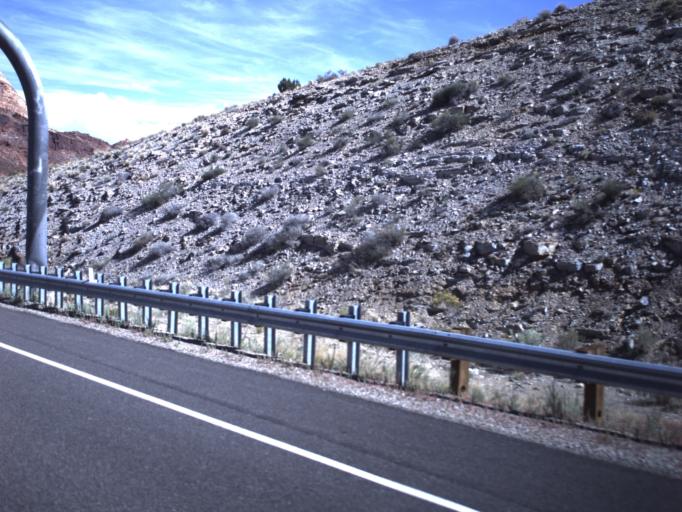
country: US
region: Utah
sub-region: Carbon County
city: East Carbon City
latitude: 38.9375
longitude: -110.4699
